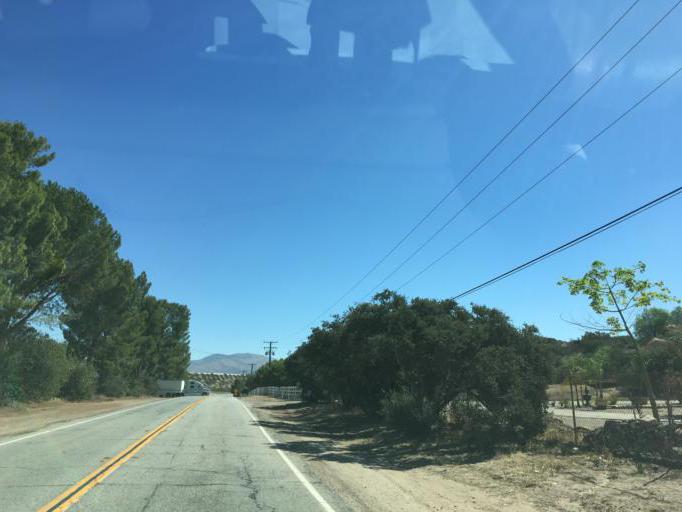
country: US
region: California
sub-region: Los Angeles County
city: Agua Dulce
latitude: 34.4798
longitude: -118.3470
